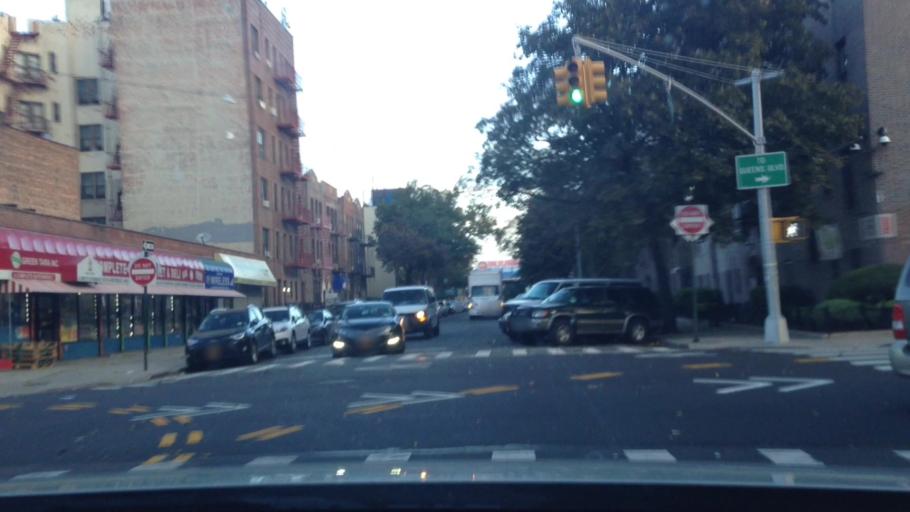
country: US
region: New York
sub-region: Queens County
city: Long Island City
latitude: 40.7408
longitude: -73.9174
